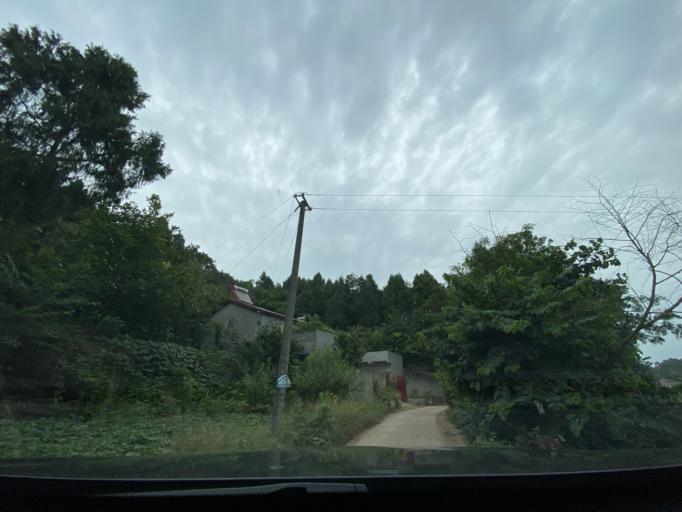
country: CN
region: Sichuan
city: Jiancheng
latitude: 30.3857
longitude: 104.4824
